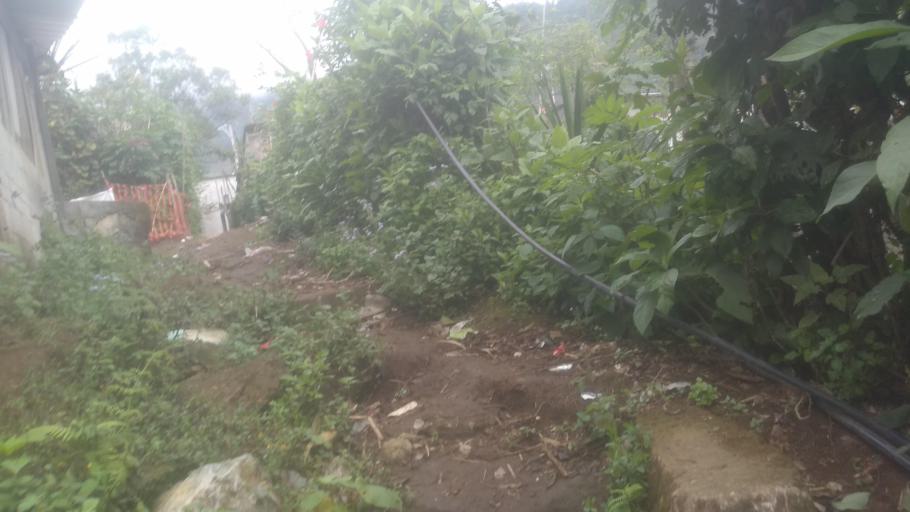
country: MX
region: Veracruz
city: Chocaman
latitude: 18.9839
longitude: -97.0644
